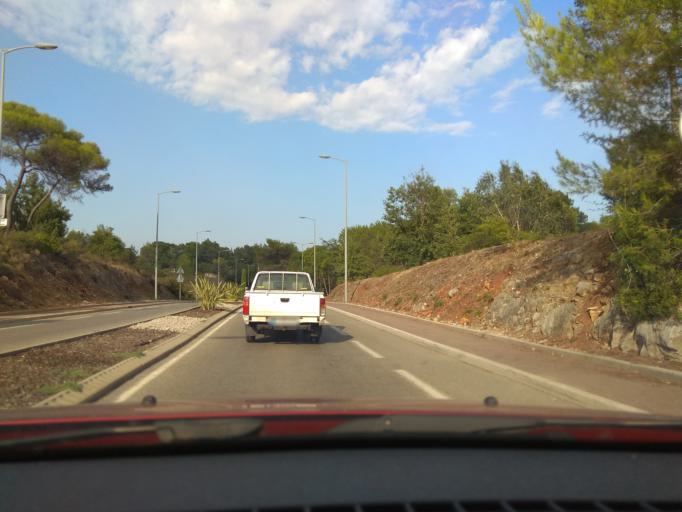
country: FR
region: Provence-Alpes-Cote d'Azur
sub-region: Departement des Alpes-Maritimes
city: Le Rouret
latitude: 43.6634
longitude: 7.0394
